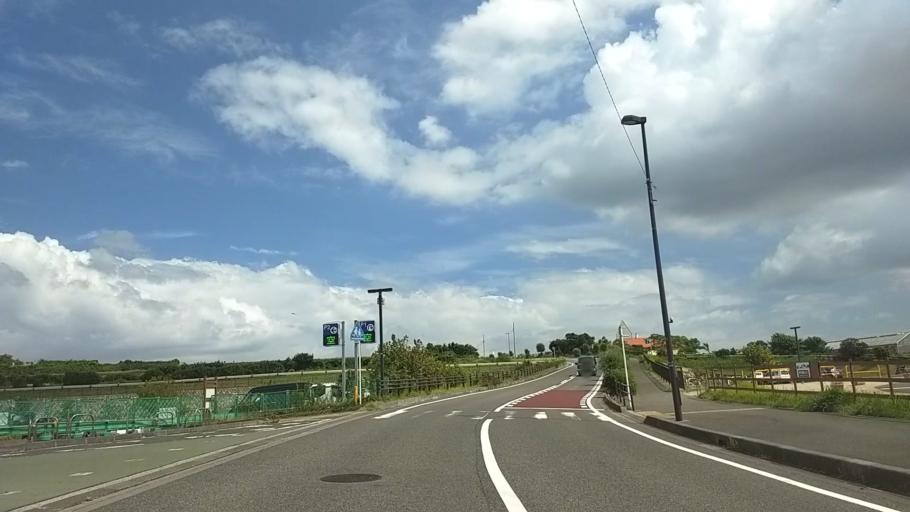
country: JP
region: Kanagawa
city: Miura
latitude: 35.1972
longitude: 139.6119
